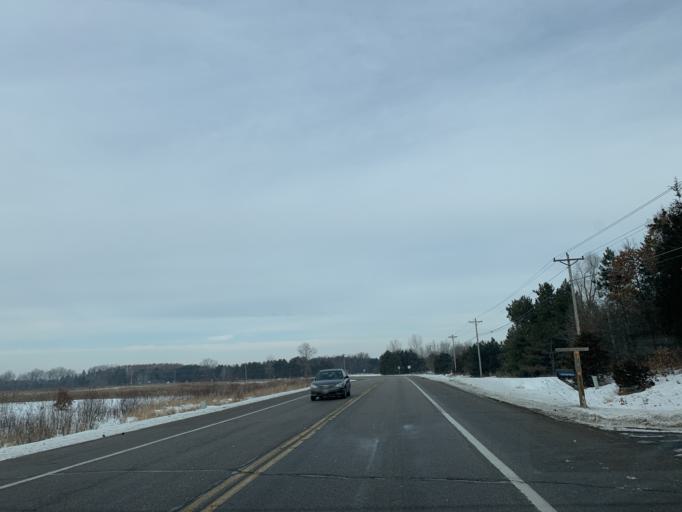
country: US
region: Minnesota
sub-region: Washington County
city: Forest Lake
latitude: 45.2846
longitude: -93.0141
